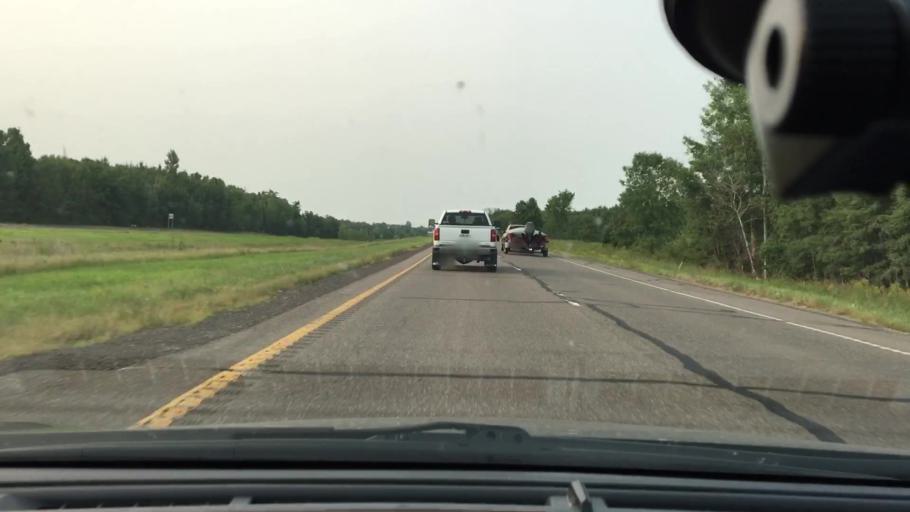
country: US
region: Minnesota
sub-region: Mille Lacs County
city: Milaca
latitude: 45.8086
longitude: -93.6533
